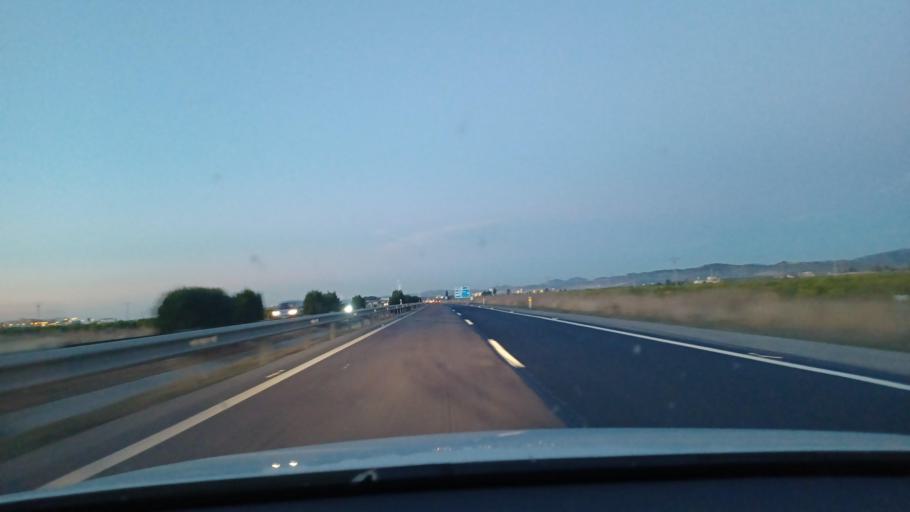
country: ES
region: Valencia
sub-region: Provincia de Castello
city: Moncofar
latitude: 39.8213
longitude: -0.1484
